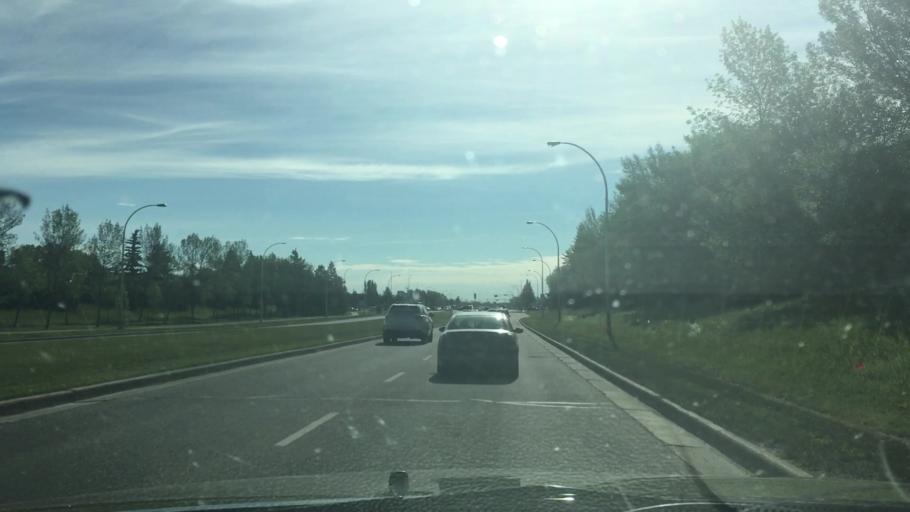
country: CA
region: Alberta
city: Edmonton
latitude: 53.4538
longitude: -113.5209
